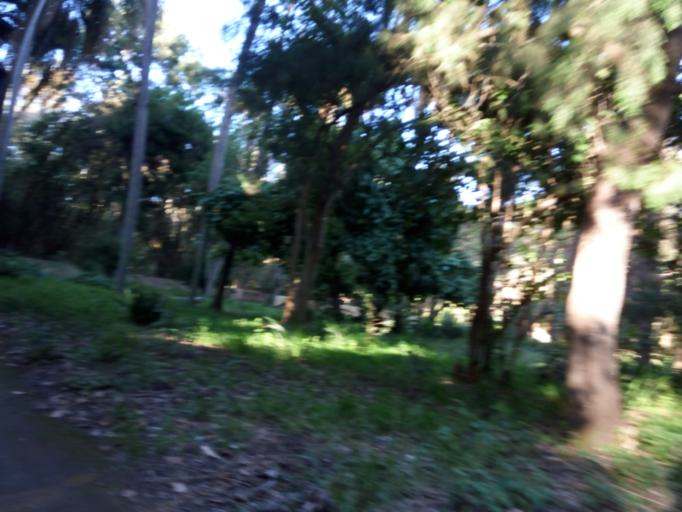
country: DZ
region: Alger
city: Algiers
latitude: 36.7477
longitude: 3.0725
